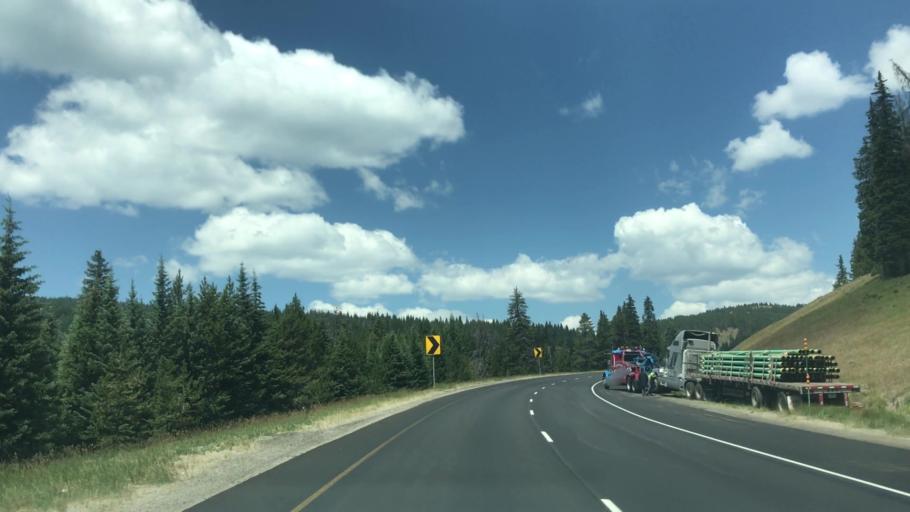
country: US
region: Colorado
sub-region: Summit County
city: Frisco
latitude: 39.5176
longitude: -106.2095
